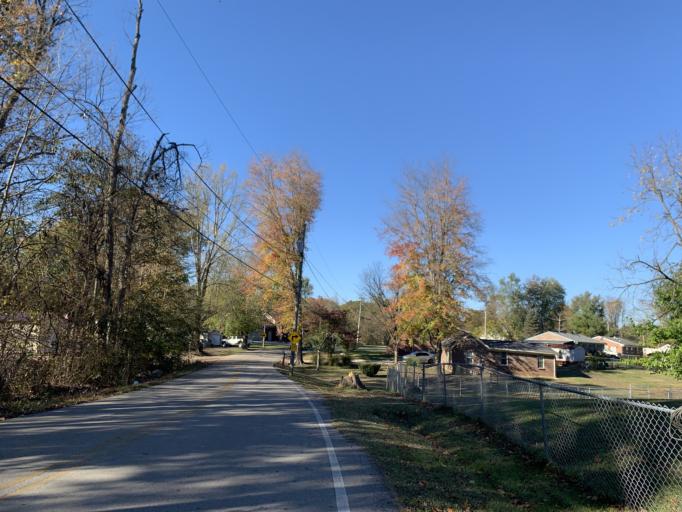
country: US
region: Kentucky
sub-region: Jefferson County
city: Pleasure Ridge Park
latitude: 38.1528
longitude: -85.8777
